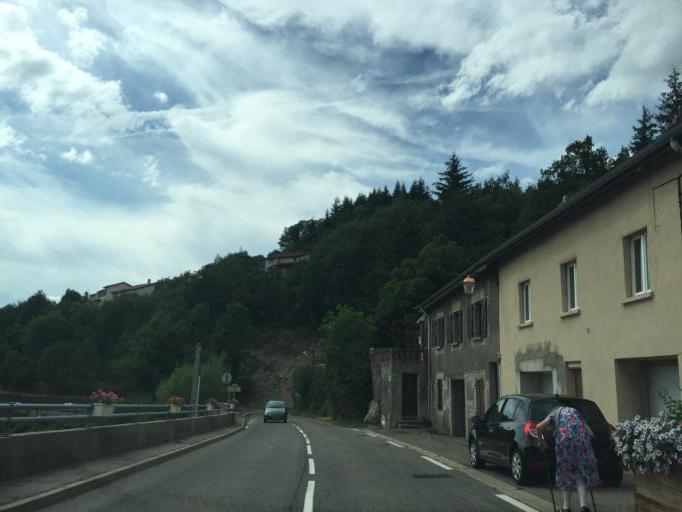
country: FR
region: Rhone-Alpes
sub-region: Departement de la Loire
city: Saint-Jean-Bonnefonds
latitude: 45.4110
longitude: 4.4383
